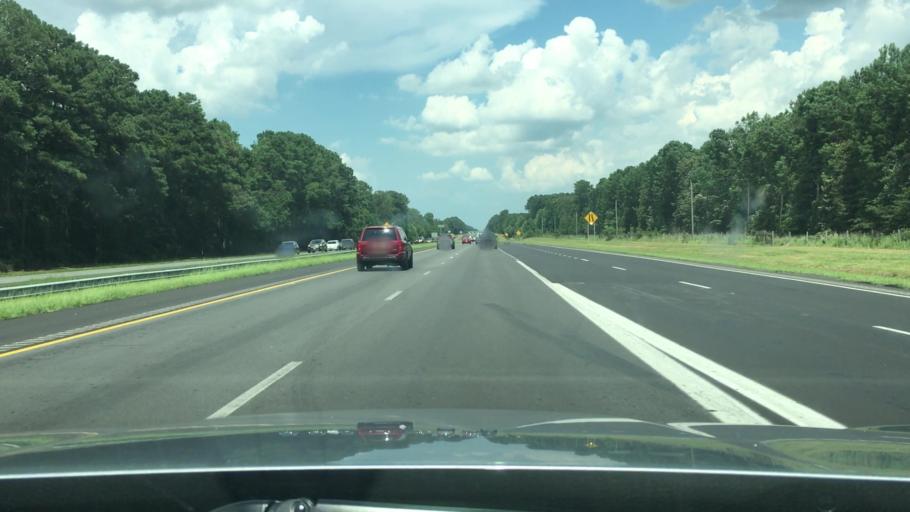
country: US
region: North Carolina
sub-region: Cumberland County
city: Eastover
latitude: 35.1289
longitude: -78.7480
